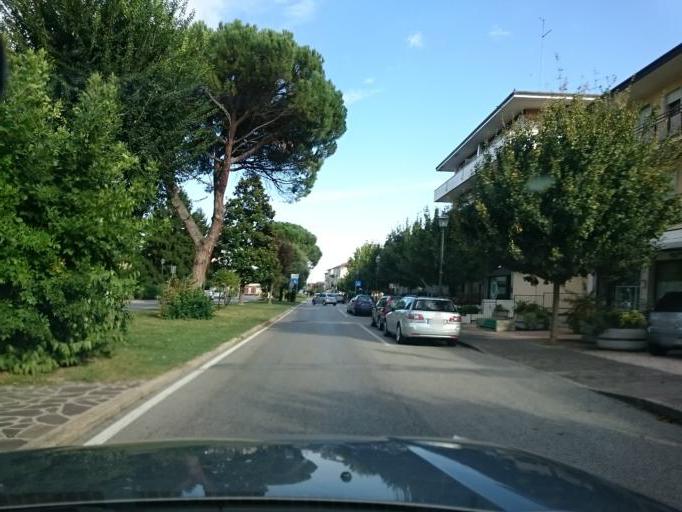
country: IT
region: Veneto
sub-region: Provincia di Padova
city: Torreglia
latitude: 45.3353
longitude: 11.7296
